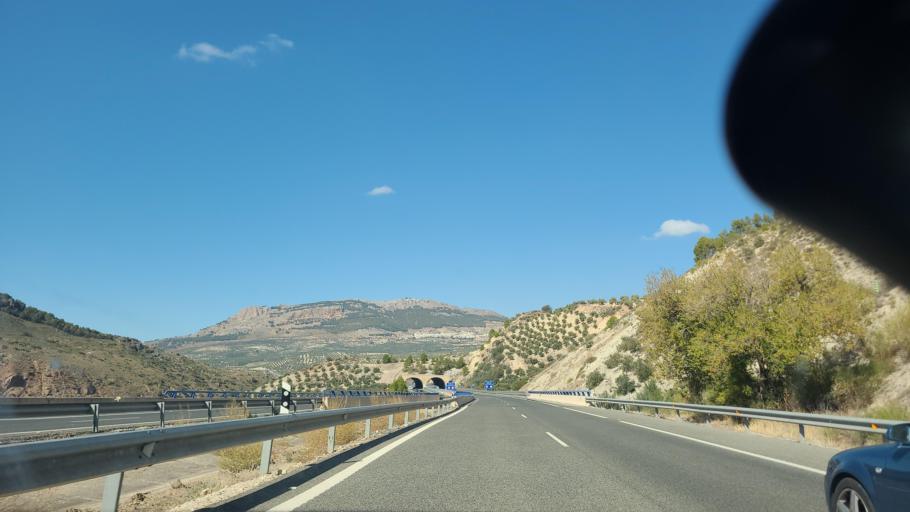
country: ES
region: Andalusia
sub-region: Provincia de Jaen
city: Pegalajar
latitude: 37.6985
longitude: -3.6340
